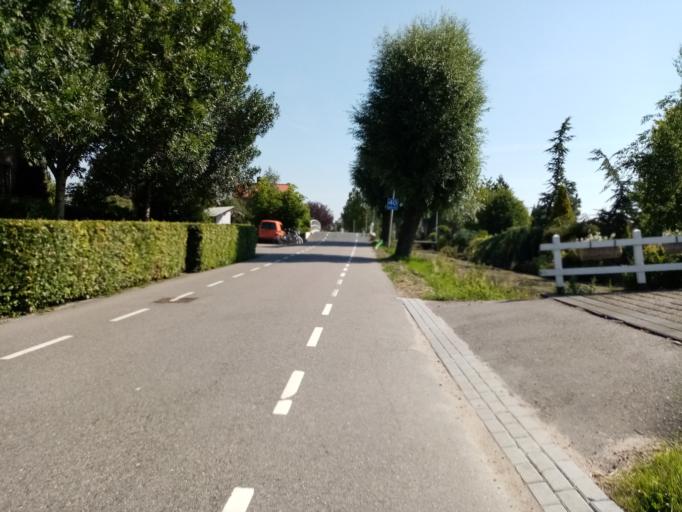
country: NL
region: South Holland
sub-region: Gemeente Kaag en Braassem
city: Leimuiden
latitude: 52.1835
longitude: 4.7175
